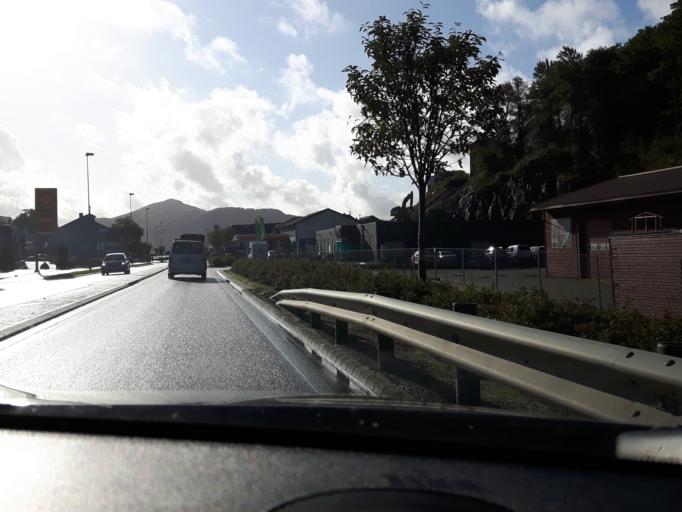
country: NO
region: Rogaland
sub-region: Gjesdal
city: Algard
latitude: 58.7682
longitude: 5.8591
